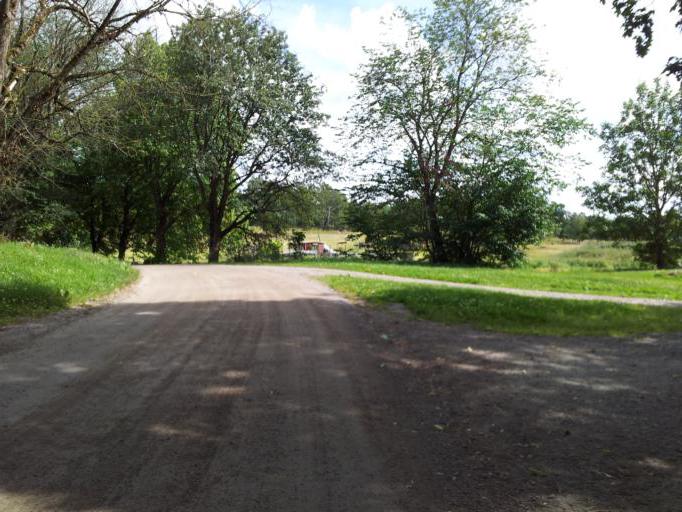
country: SE
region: Stockholm
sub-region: Norrtalje Kommun
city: Nykvarn
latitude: 59.8983
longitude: 18.2014
